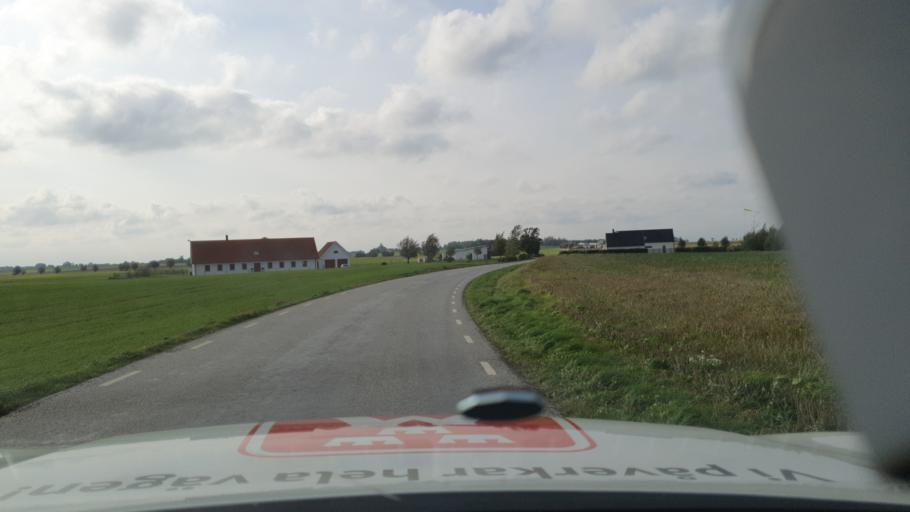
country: SE
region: Skane
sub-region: Malmo
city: Oxie
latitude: 55.4620
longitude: 13.0951
